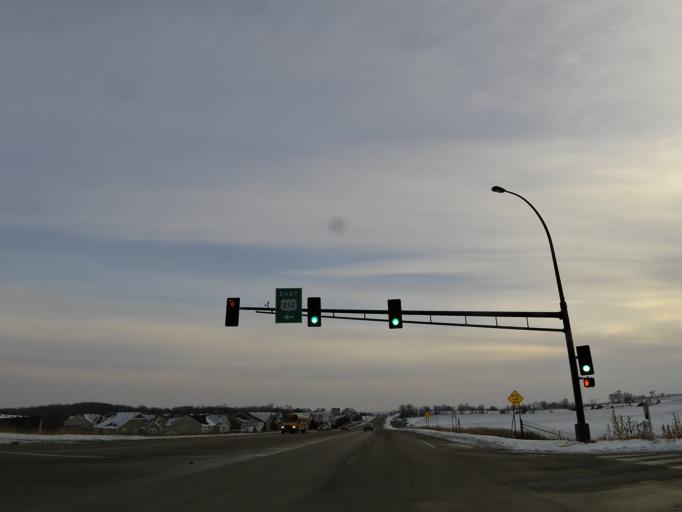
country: US
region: Minnesota
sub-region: Carver County
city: Carver
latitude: 44.7769
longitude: -93.6427
